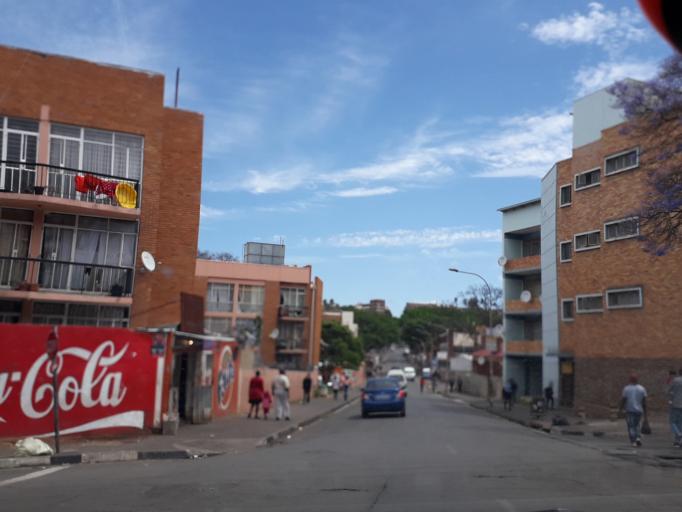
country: ZA
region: Gauteng
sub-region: City of Johannesburg Metropolitan Municipality
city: Johannesburg
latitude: -26.1783
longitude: 28.0701
